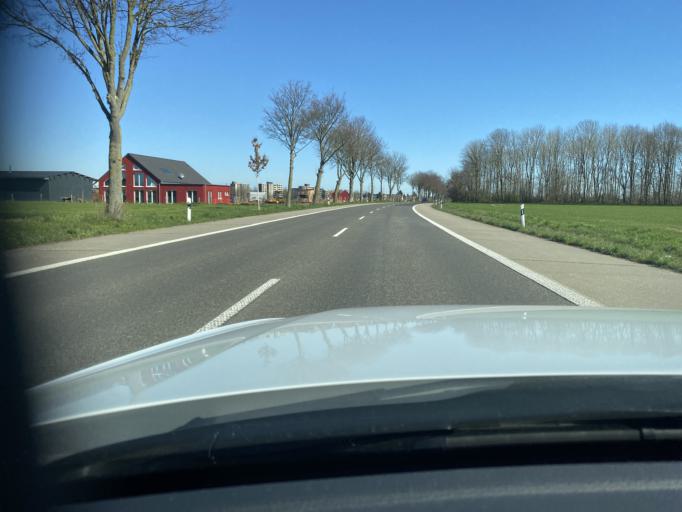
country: DE
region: North Rhine-Westphalia
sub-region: Regierungsbezirk Dusseldorf
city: Neubrueck
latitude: 51.1499
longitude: 6.6587
